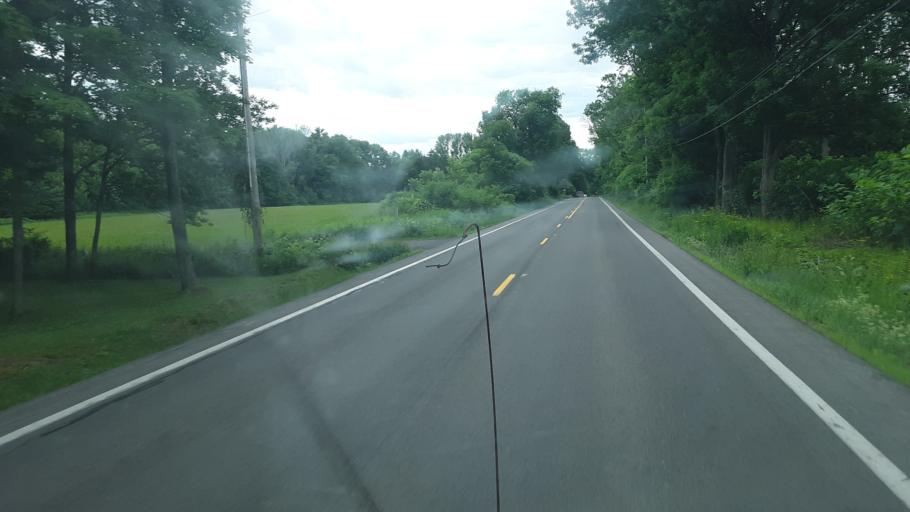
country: US
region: New York
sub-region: Oneida County
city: Rome
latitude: 43.3218
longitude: -75.4766
